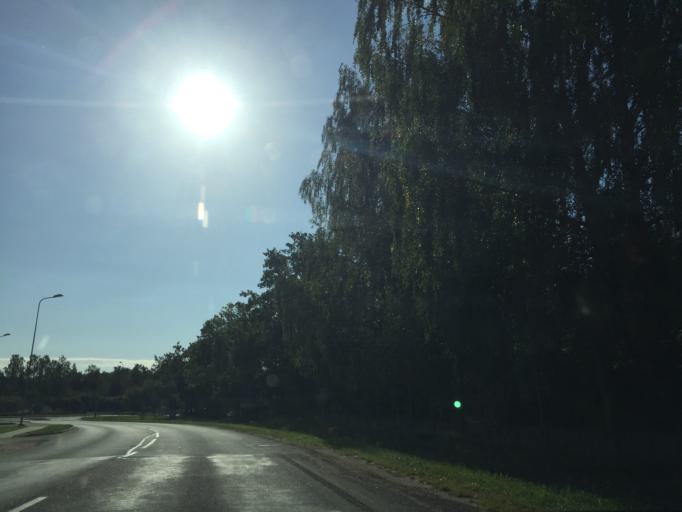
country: LV
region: Limbazu Rajons
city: Limbazi
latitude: 57.5102
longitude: 24.6957
